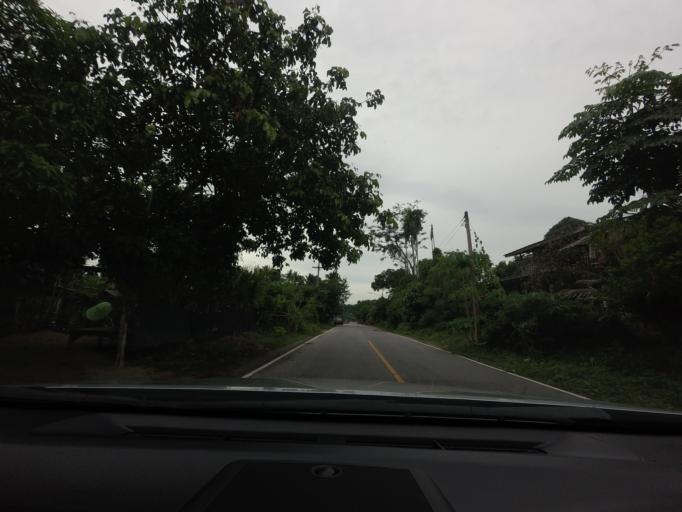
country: TH
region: Narathiwat
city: Rueso
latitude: 6.4144
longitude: 101.5240
